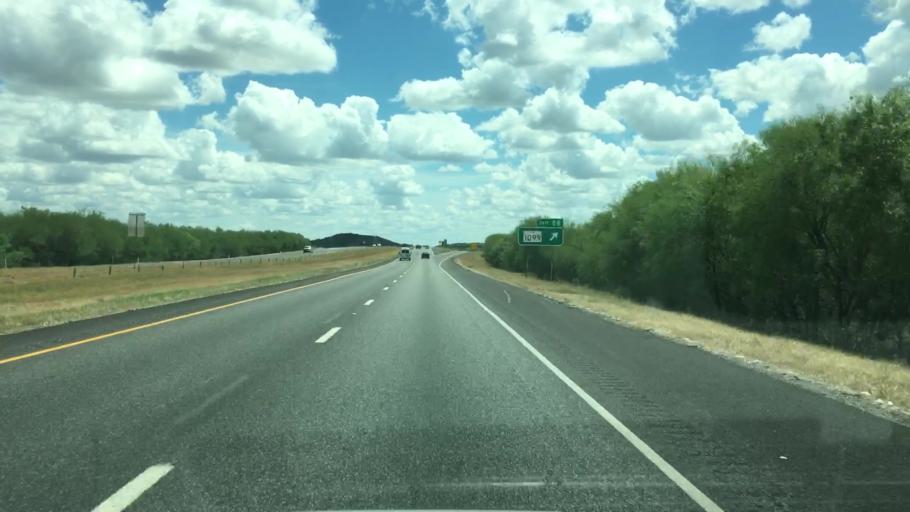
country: US
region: Texas
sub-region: Atascosa County
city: Pleasanton
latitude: 28.7398
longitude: -98.2915
